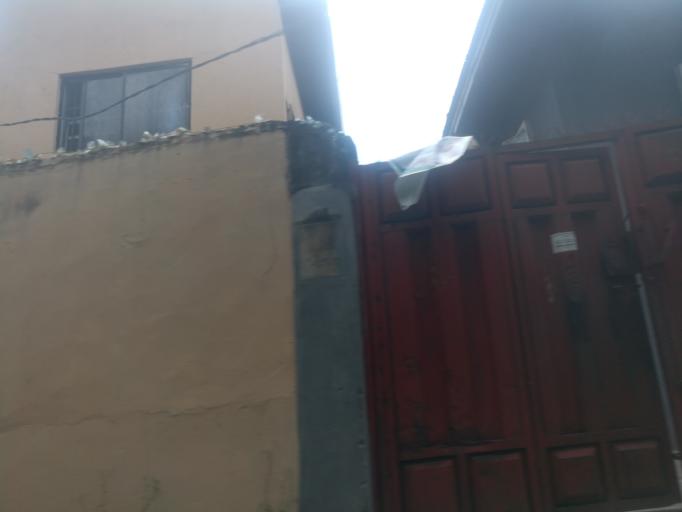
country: NG
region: Lagos
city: Somolu
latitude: 6.5581
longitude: 3.3852
